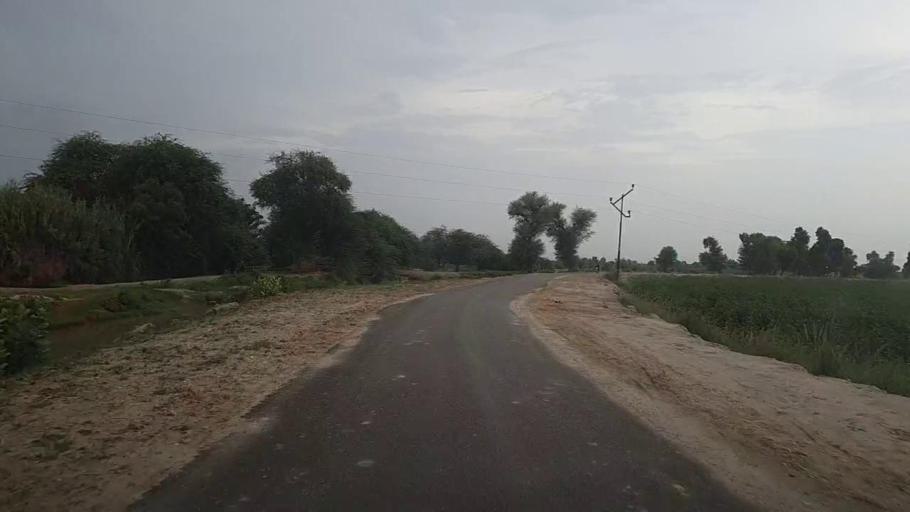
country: PK
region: Sindh
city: Karaundi
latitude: 26.9627
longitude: 68.3657
